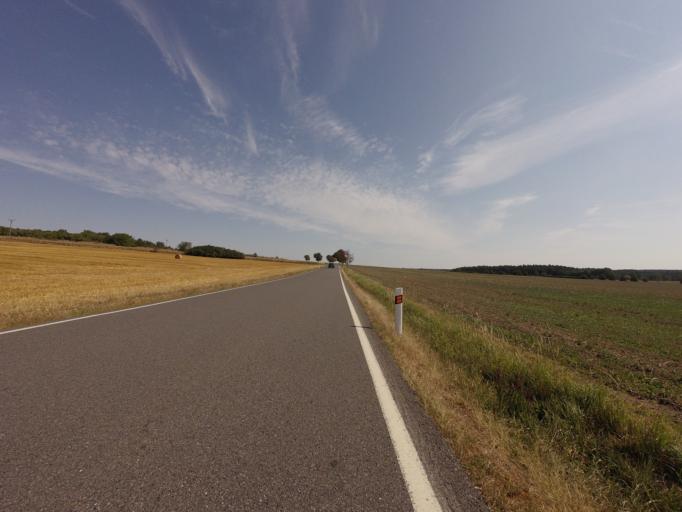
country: CZ
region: Jihocesky
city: Bernartice
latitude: 49.3478
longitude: 14.3713
